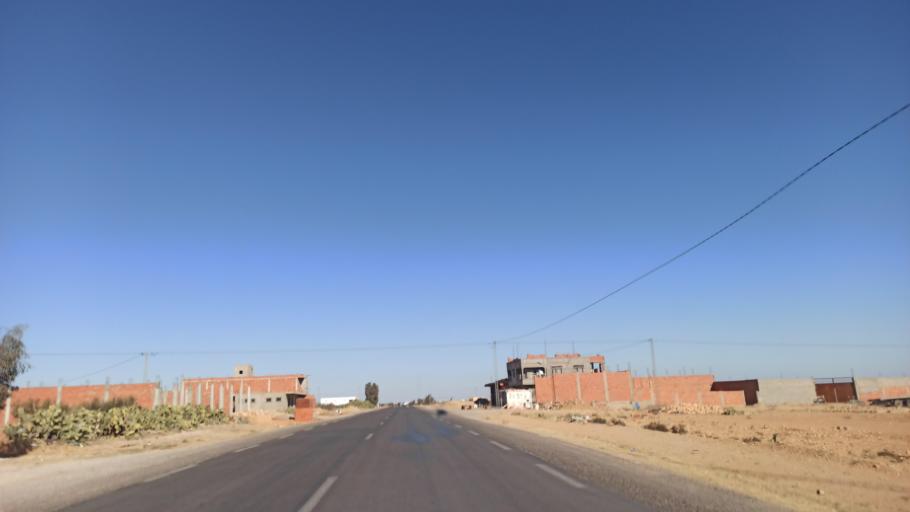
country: TN
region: Sidi Bu Zayd
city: Bi'r al Hufayy
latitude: 34.9500
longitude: 9.2113
